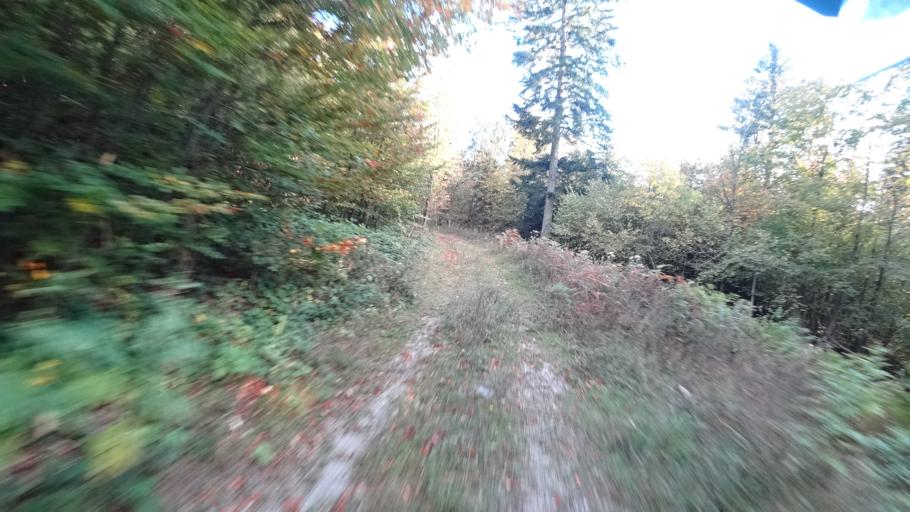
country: HR
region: Karlovacka
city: Plaski
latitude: 45.0227
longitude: 15.4328
